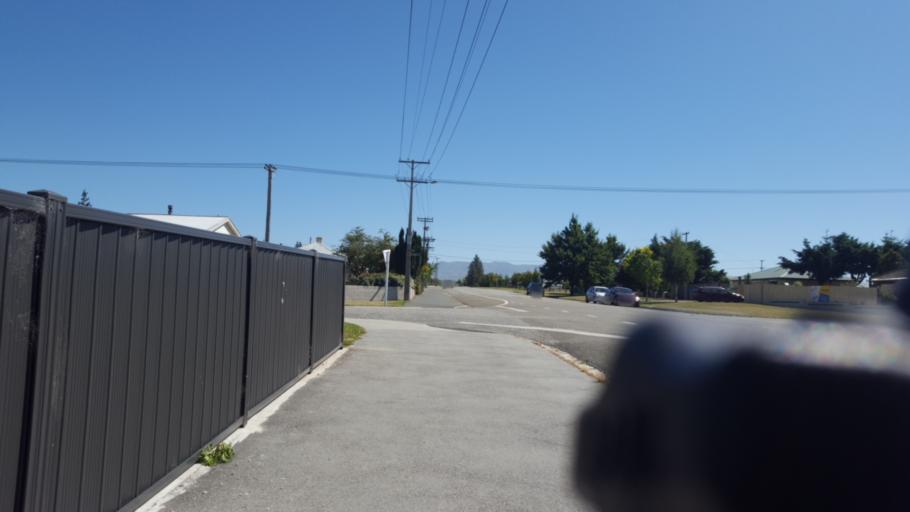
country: NZ
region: Otago
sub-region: Dunedin City
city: Dunedin
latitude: -45.1271
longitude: 170.1005
